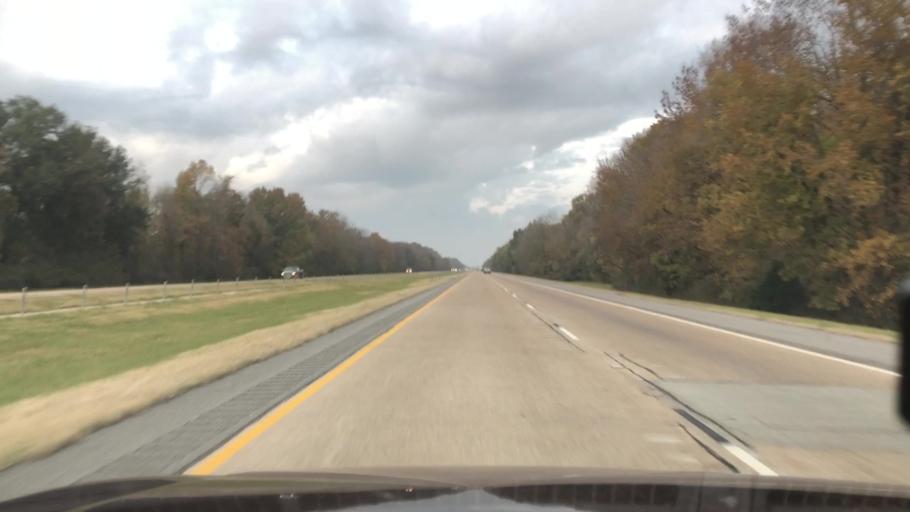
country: US
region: Louisiana
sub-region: Madison Parish
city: Tallulah
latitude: 32.3389
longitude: -91.0673
